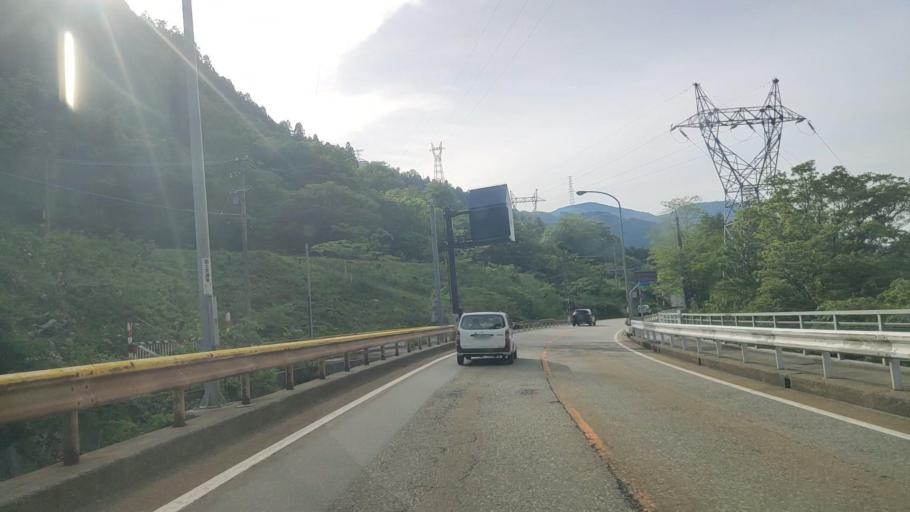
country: JP
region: Toyama
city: Yatsuomachi-higashikumisaka
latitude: 36.4530
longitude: 137.2549
